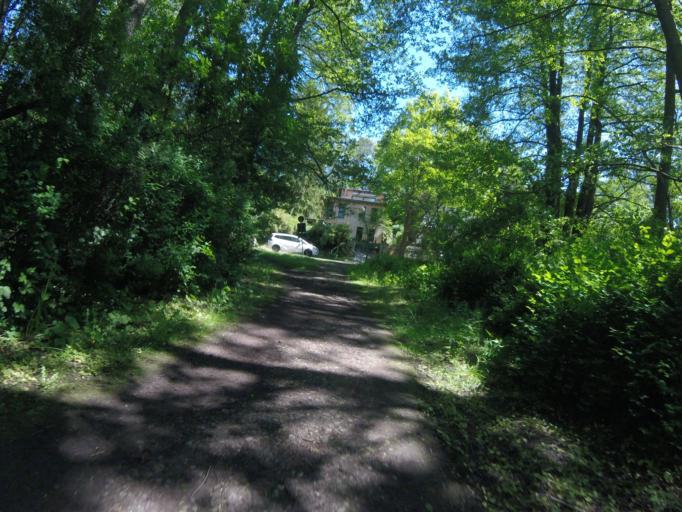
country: DE
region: Brandenburg
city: Teupitz
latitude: 52.1328
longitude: 13.6129
